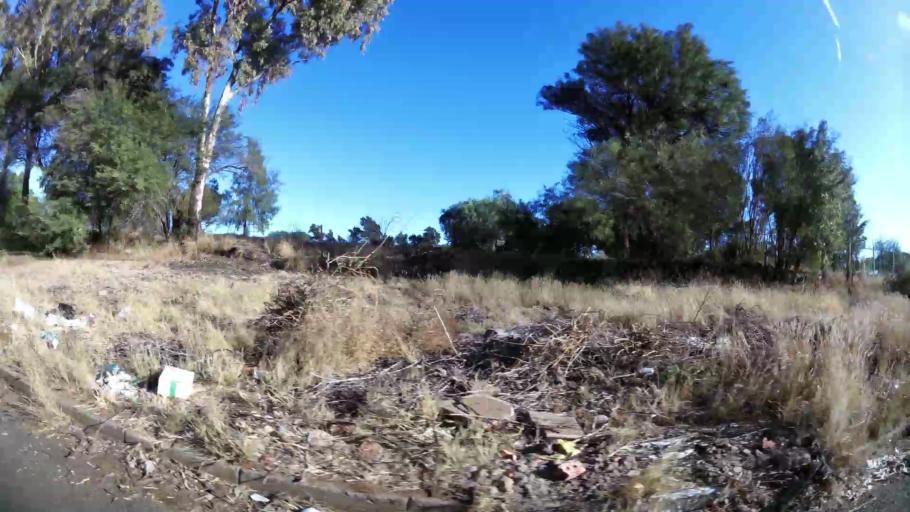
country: ZA
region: Northern Cape
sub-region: Frances Baard District Municipality
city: Kimberley
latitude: -28.7548
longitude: 24.7782
